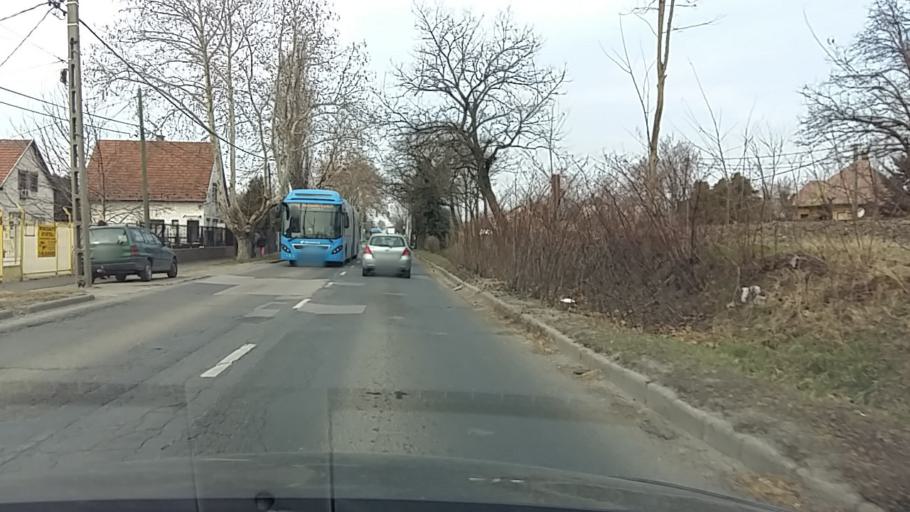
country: HU
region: Budapest
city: Budapest XVIII. keruelet
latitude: 47.4097
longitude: 19.1784
